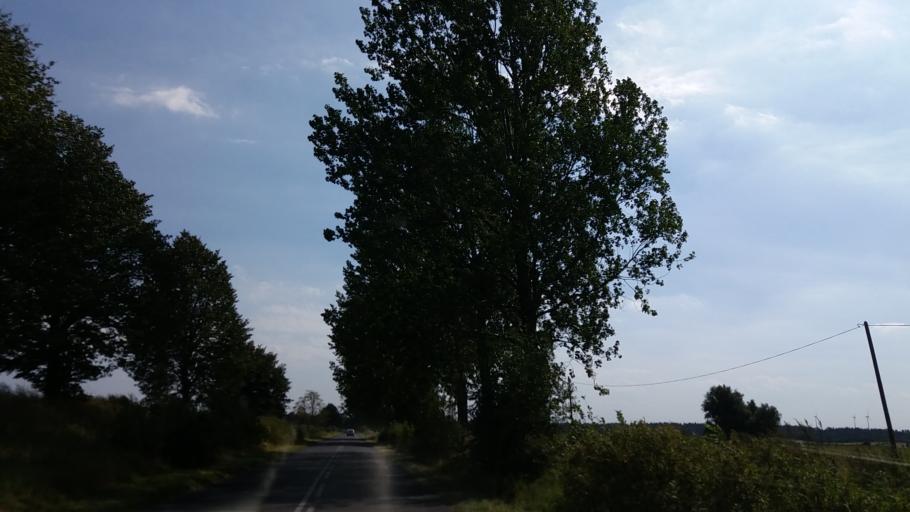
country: PL
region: West Pomeranian Voivodeship
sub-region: Powiat choszczenski
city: Krzecin
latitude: 53.1024
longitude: 15.4624
